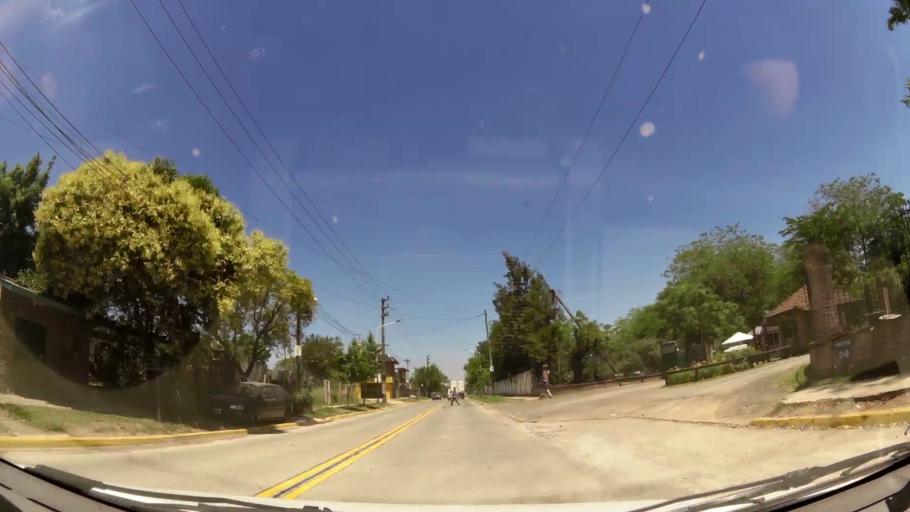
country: AR
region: Buenos Aires
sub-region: Partido de Merlo
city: Merlo
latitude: -34.6463
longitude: -58.7189
